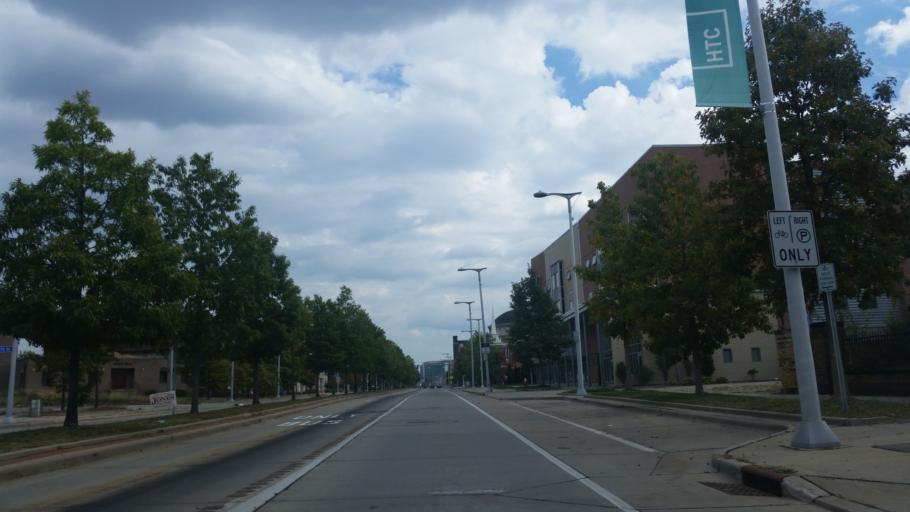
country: US
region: Ohio
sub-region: Cuyahoga County
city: Bratenahl
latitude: 41.5039
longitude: -81.6383
